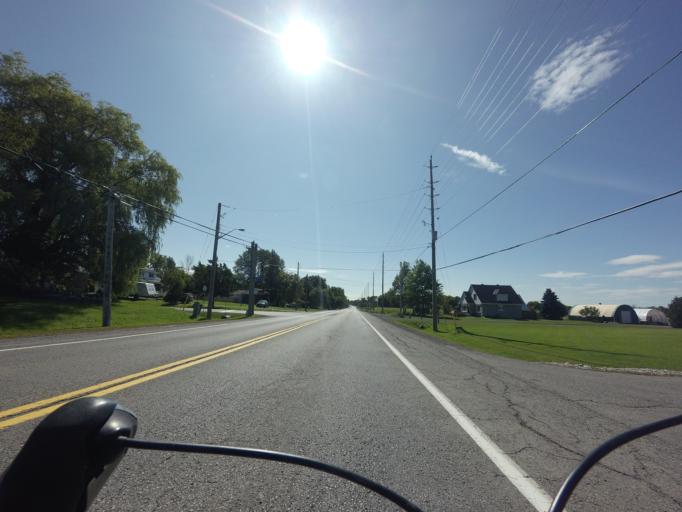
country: CA
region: Ontario
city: Bells Corners
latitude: 45.2655
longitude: -75.8287
